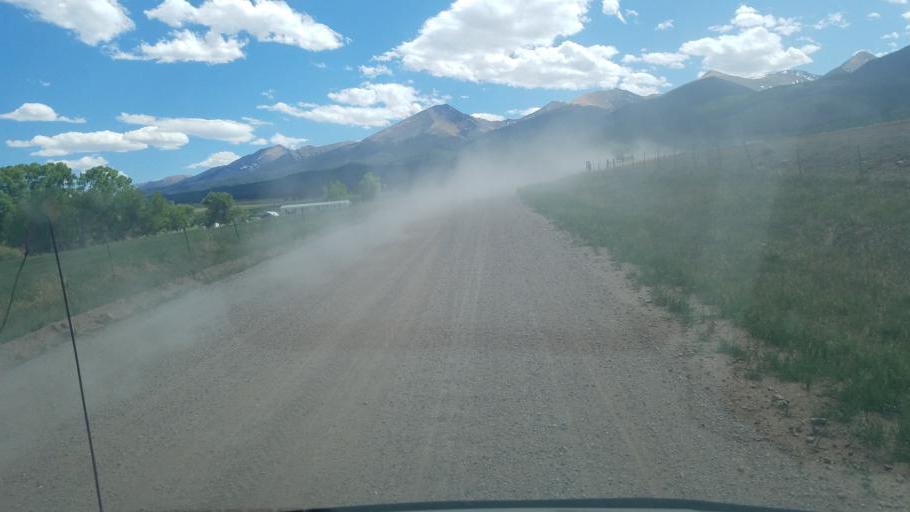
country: US
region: Colorado
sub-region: Custer County
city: Westcliffe
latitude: 38.2601
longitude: -105.6140
